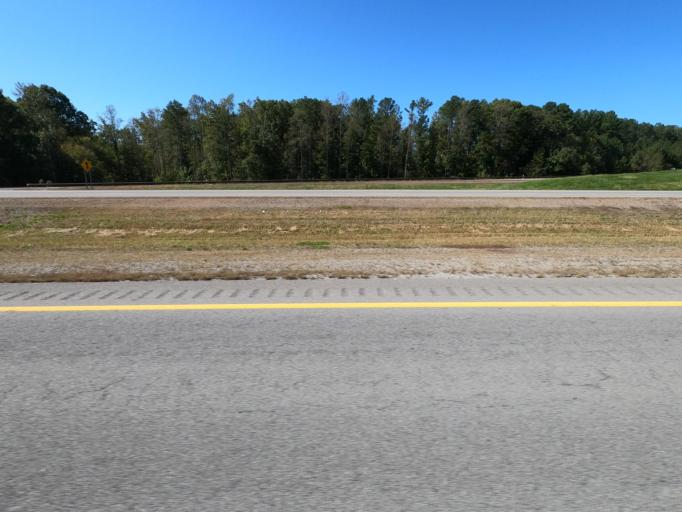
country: US
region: Tennessee
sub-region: Williamson County
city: Fairview
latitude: 35.8758
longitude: -87.0957
